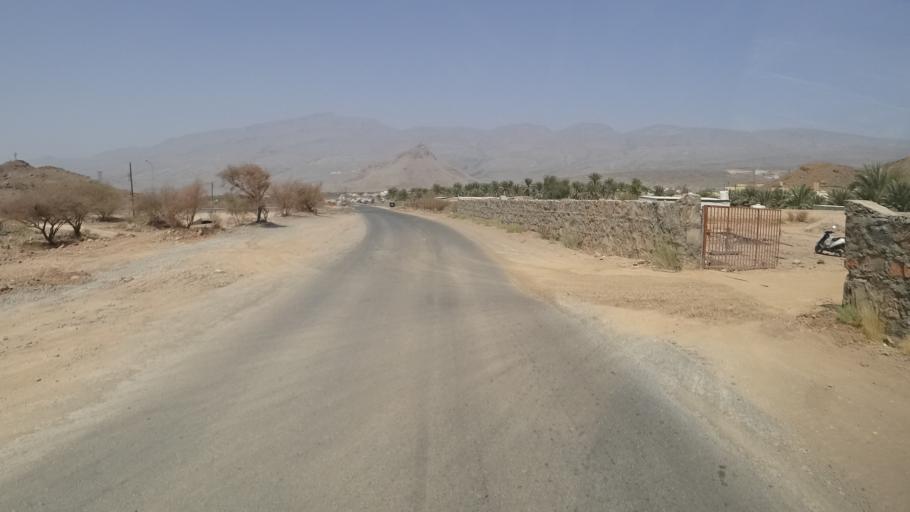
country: OM
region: Muhafazat ad Dakhiliyah
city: Bahla'
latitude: 23.0810
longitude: 57.3133
